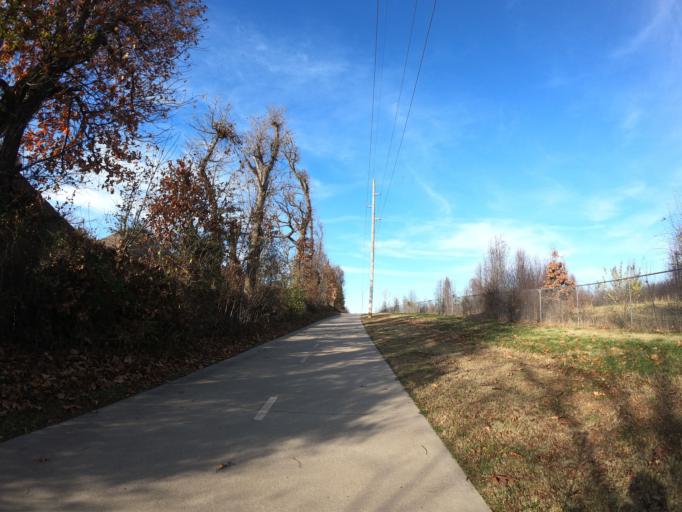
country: US
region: Arkansas
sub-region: Benton County
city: Lowell
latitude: 36.2891
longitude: -94.1654
